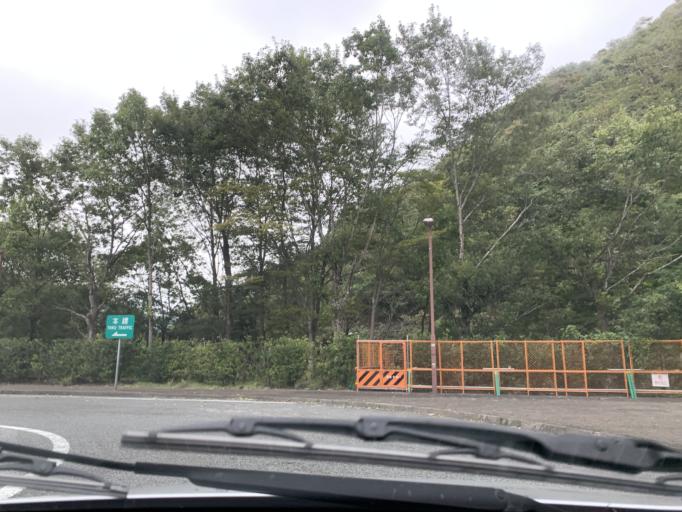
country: JP
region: Shizuoka
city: Gotemba
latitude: 35.3567
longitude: 139.0170
